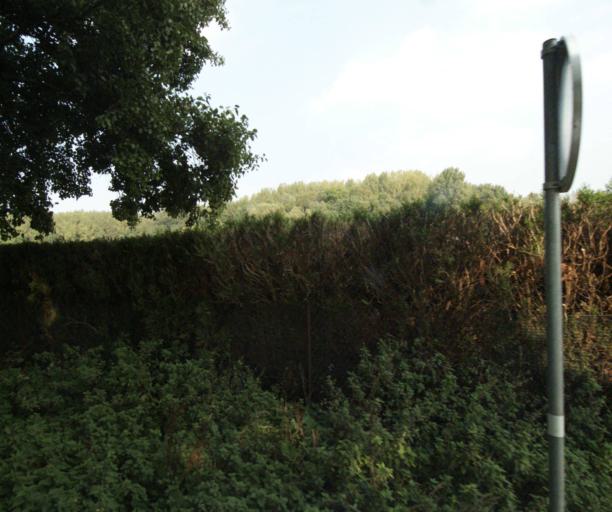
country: FR
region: Nord-Pas-de-Calais
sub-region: Departement du Nord
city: Emmerin
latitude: 50.5826
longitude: 2.9891
